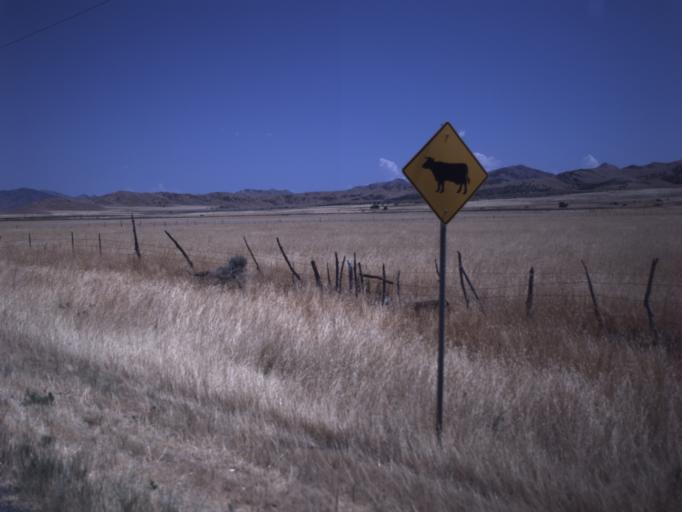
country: US
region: Utah
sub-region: Millard County
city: Delta
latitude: 39.3904
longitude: -112.3356
